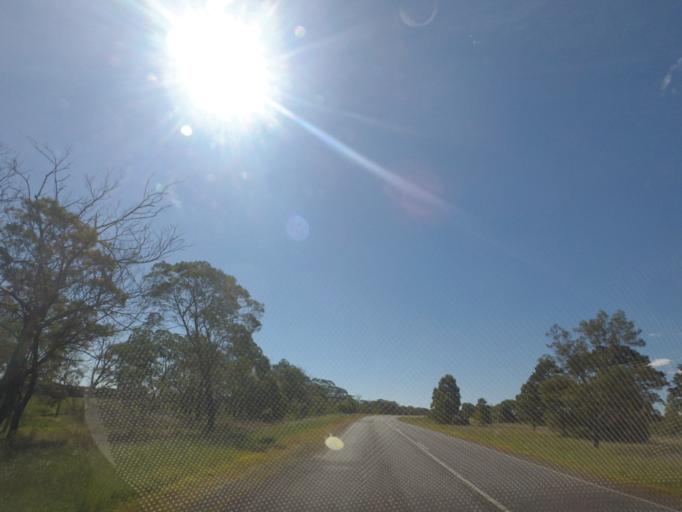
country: AU
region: Victoria
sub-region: Moorabool
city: Bacchus Marsh
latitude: -37.6361
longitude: 144.2180
